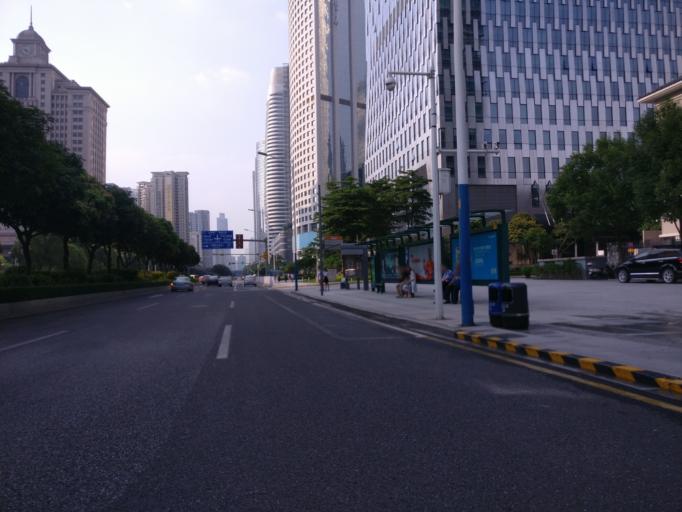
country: CN
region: Guangdong
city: Wushan
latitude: 23.1203
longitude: 113.3160
